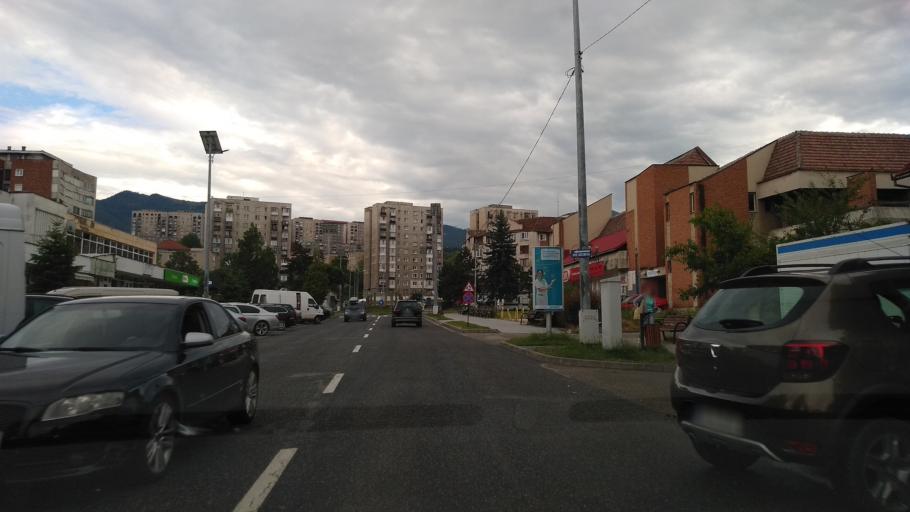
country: RO
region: Hunedoara
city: Vulcan
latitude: 45.3760
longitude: 23.2951
